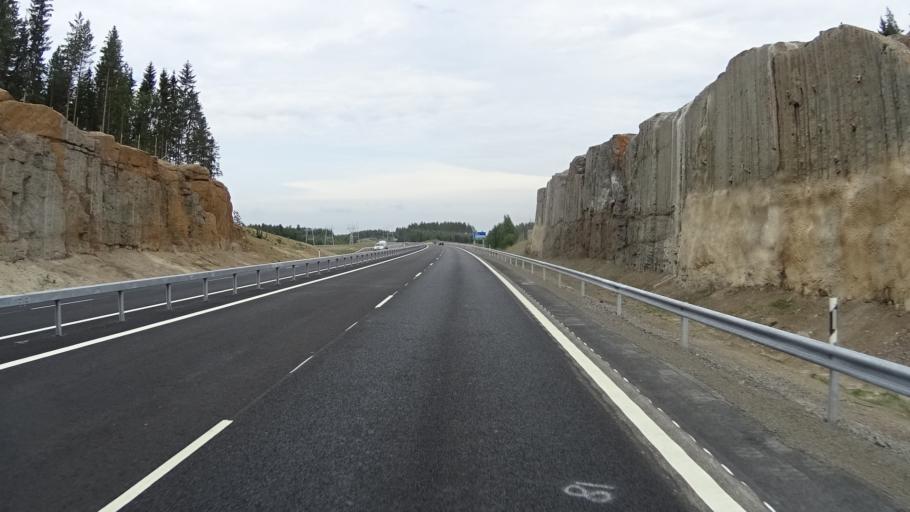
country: FI
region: South Karelia
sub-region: Lappeenranta
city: Lemi
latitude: 60.9637
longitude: 27.8501
